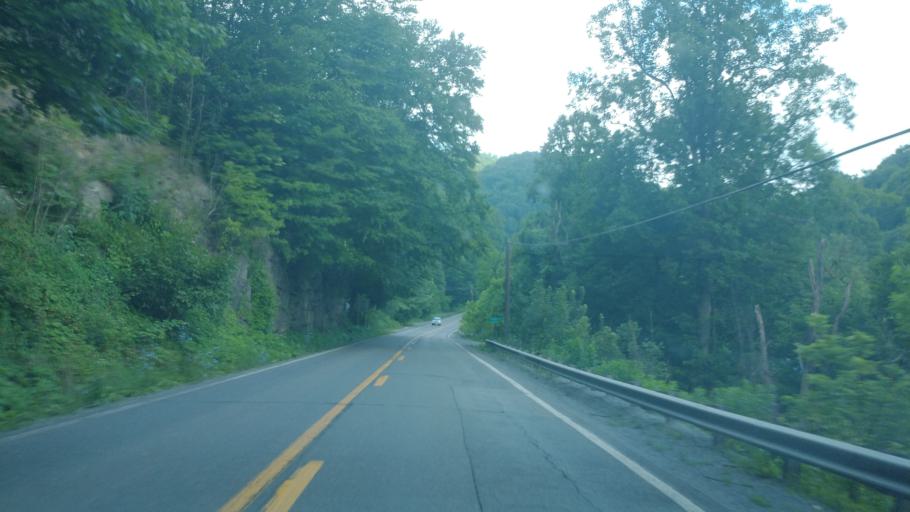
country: US
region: West Virginia
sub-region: Mercer County
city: Bluewell
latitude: 37.3857
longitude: -81.4171
